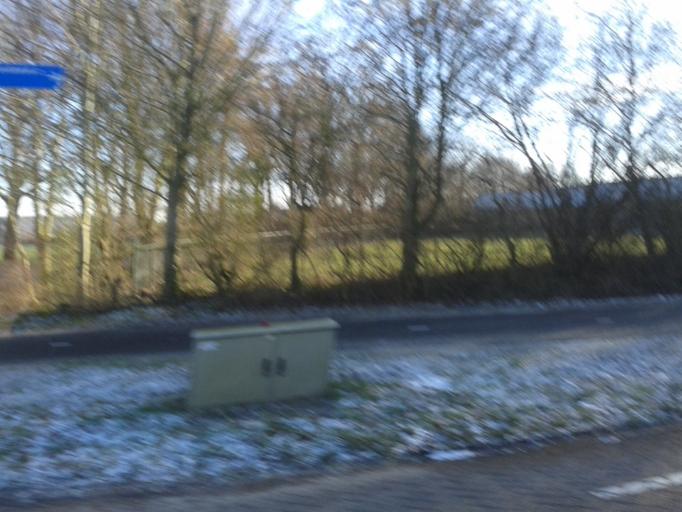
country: NL
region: North Brabant
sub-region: Gemeente Hilvarenbeek
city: Hilvarenbeek
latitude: 51.5050
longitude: 5.1603
